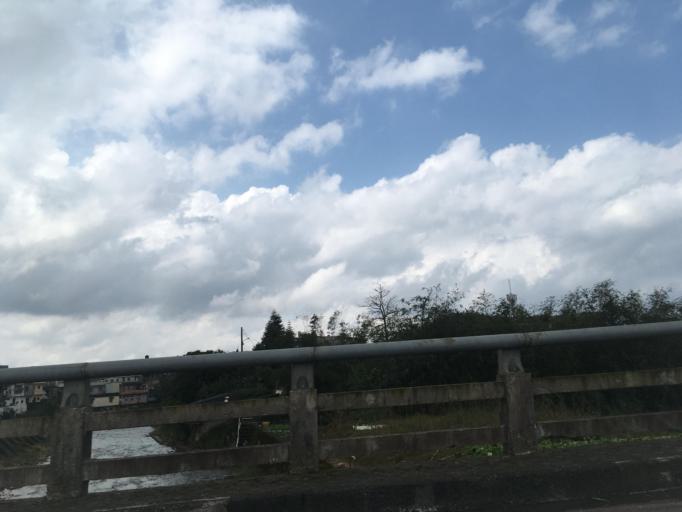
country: TW
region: Taiwan
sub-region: Keelung
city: Keelung
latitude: 25.0159
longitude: 121.9476
